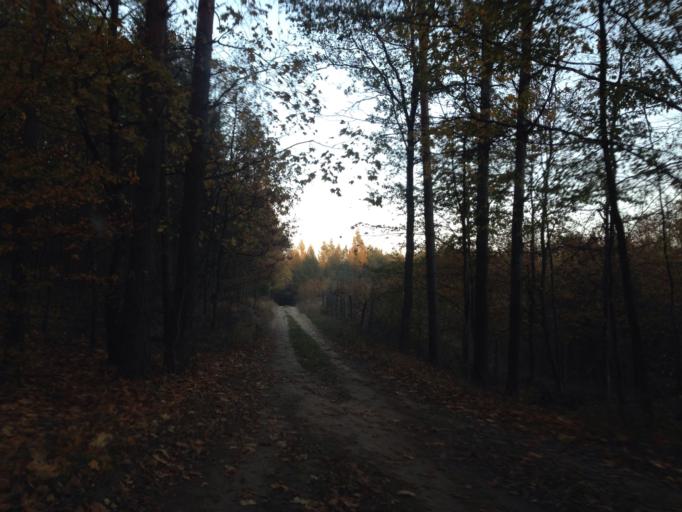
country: PL
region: Kujawsko-Pomorskie
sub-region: Powiat brodnicki
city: Gorzno
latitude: 53.2191
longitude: 19.7195
